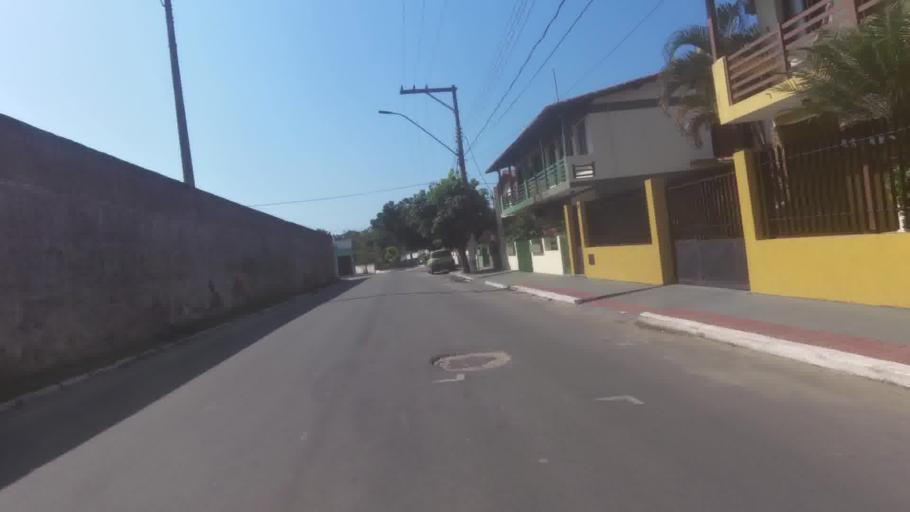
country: BR
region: Espirito Santo
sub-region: Itapemirim
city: Itapemirim
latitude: -21.0079
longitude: -40.8098
